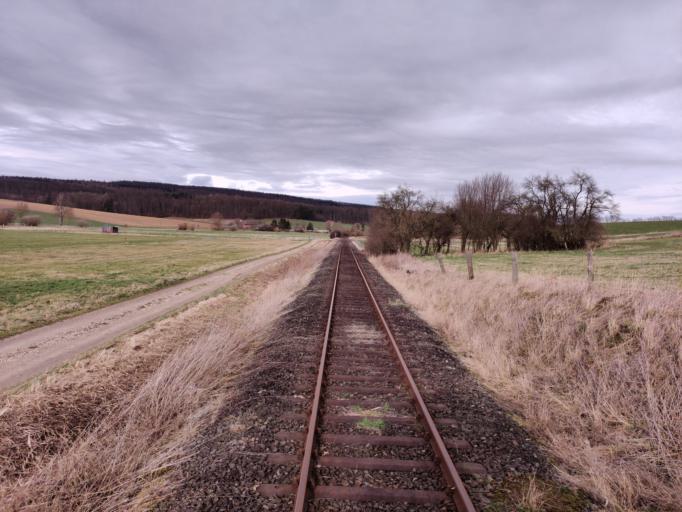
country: DE
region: Lower Saxony
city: Bockenem
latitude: 52.0401
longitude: 10.1223
